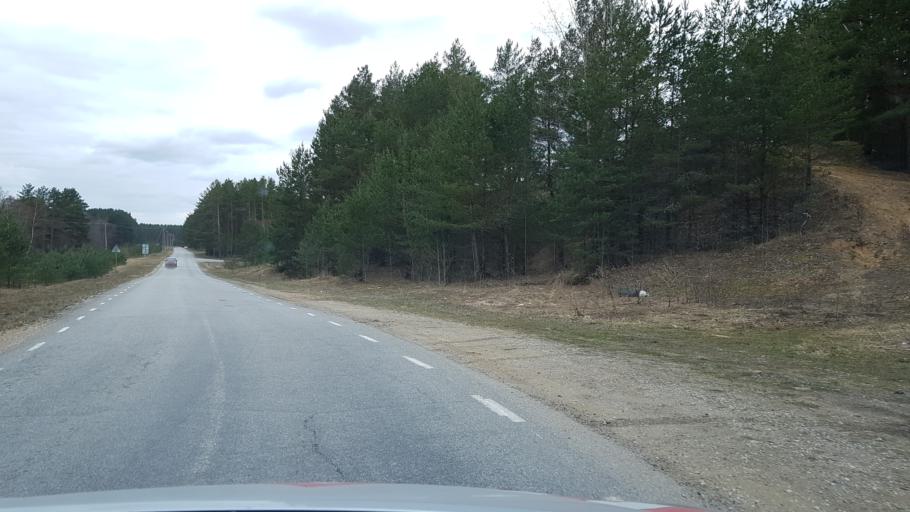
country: EE
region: Ida-Virumaa
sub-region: Narva linn
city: Narva
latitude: 59.4288
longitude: 28.1229
